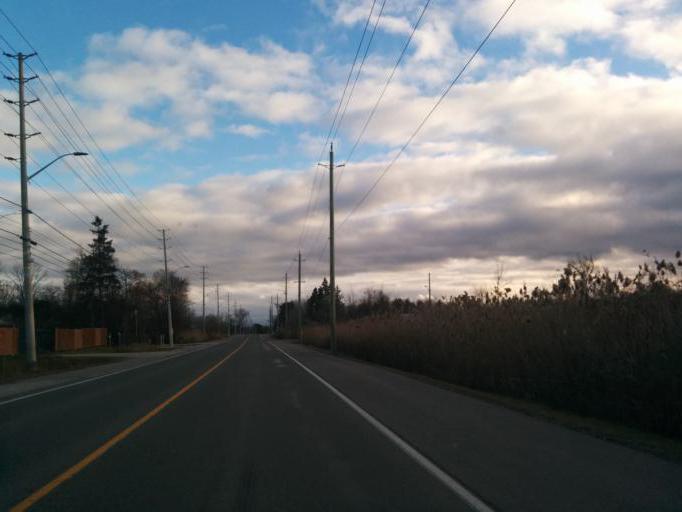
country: CA
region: Ontario
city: Oakville
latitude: 43.4882
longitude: -79.6347
